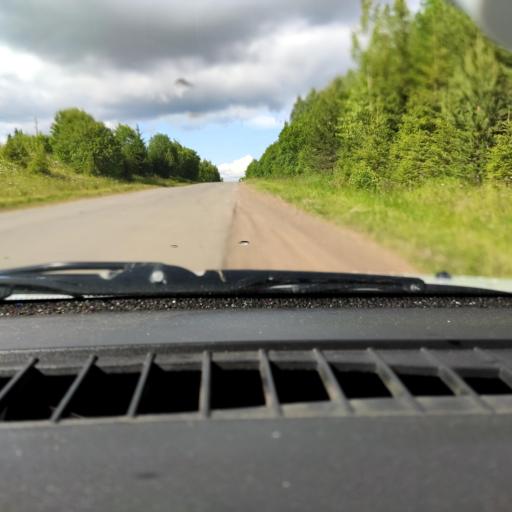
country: RU
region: Perm
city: Uinskoye
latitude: 57.1226
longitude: 56.5538
